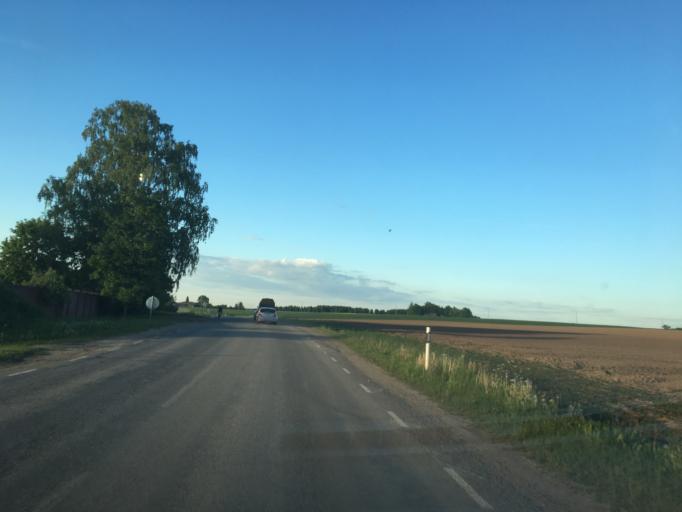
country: EE
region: Tartu
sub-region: UElenurme vald
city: Ulenurme
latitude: 58.2423
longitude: 26.6672
